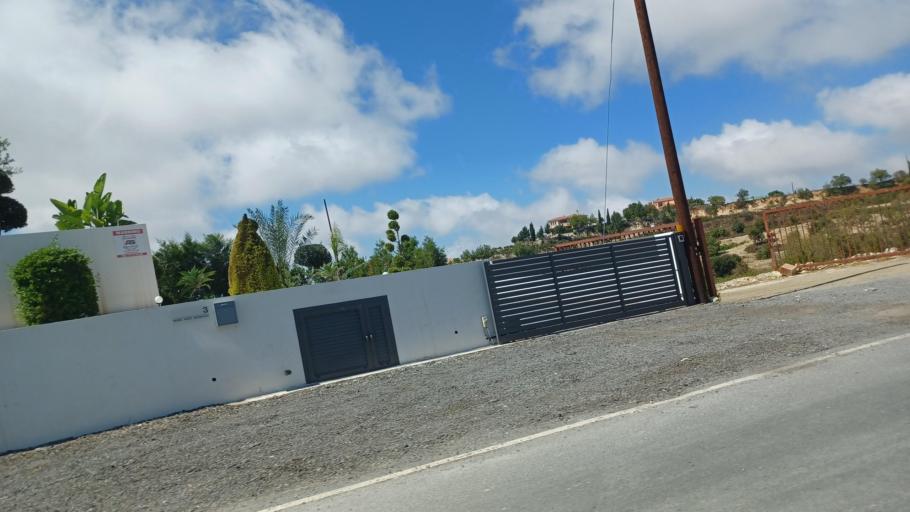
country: CY
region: Pafos
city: Tala
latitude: 34.8531
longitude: 32.4604
